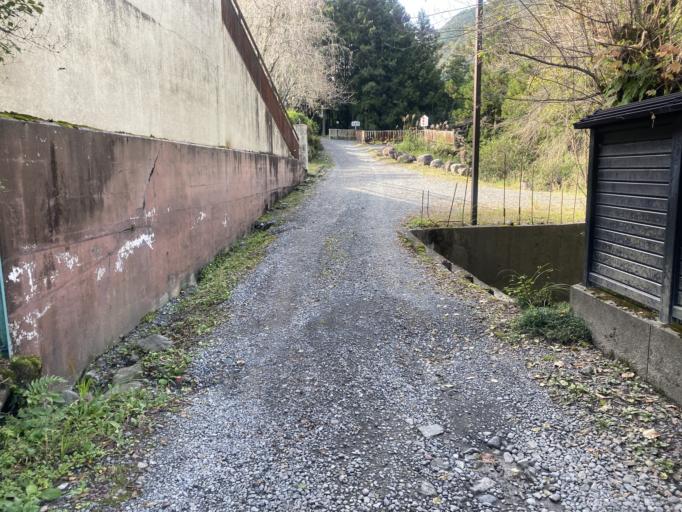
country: JP
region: Shizuoka
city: Fujinomiya
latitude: 35.3793
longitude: 138.4277
